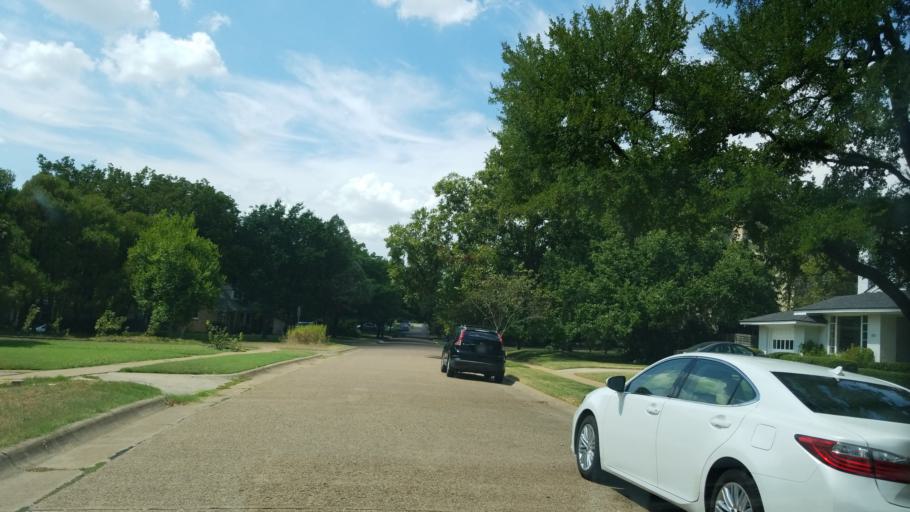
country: US
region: Texas
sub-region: Dallas County
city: Cockrell Hill
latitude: 32.7583
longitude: -96.8538
